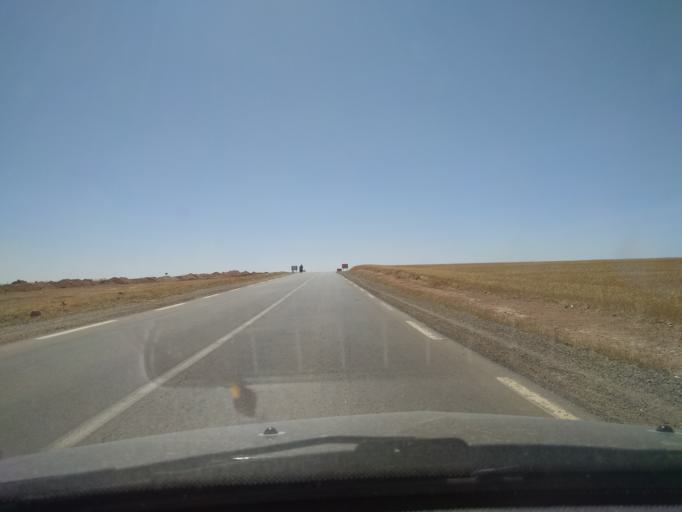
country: DZ
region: Tiaret
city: Frenda
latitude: 34.8946
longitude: 1.1689
